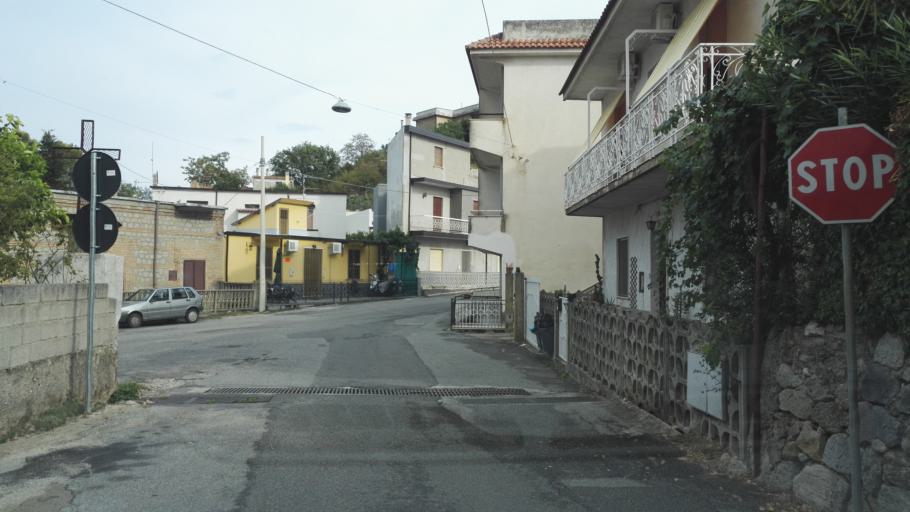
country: IT
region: Calabria
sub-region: Provincia di Reggio Calabria
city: Stignano
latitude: 38.4204
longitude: 16.4692
